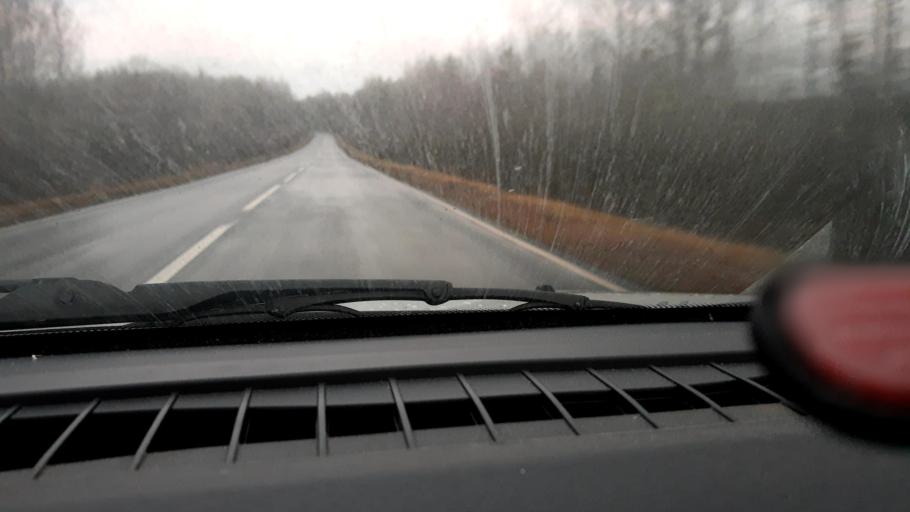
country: RU
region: Nizjnij Novgorod
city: Uren'
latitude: 57.2465
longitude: 45.5937
